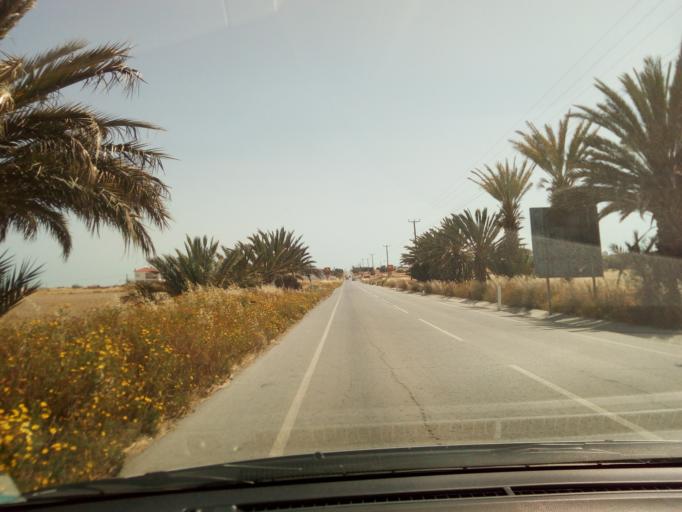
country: CY
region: Larnaka
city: Athienou
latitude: 35.0539
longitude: 33.5340
